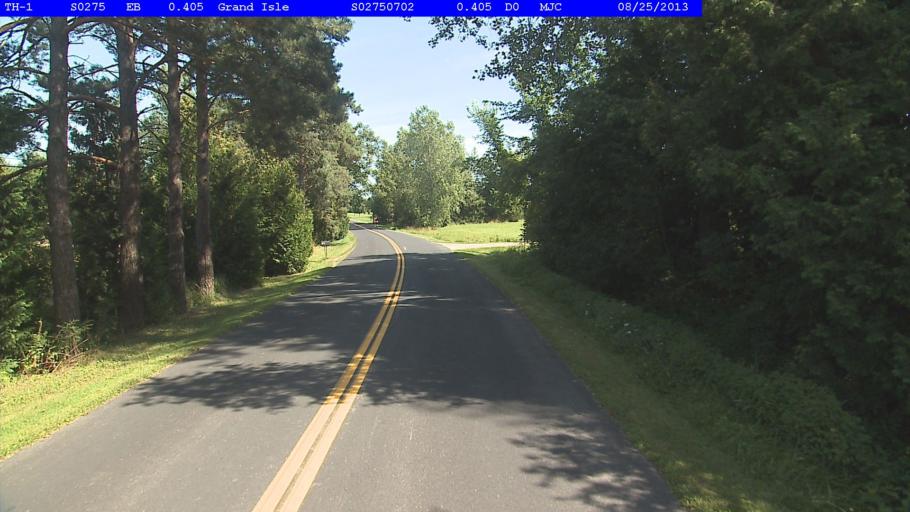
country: US
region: New York
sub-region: Clinton County
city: Cumberland Head
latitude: 44.7064
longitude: -73.3442
